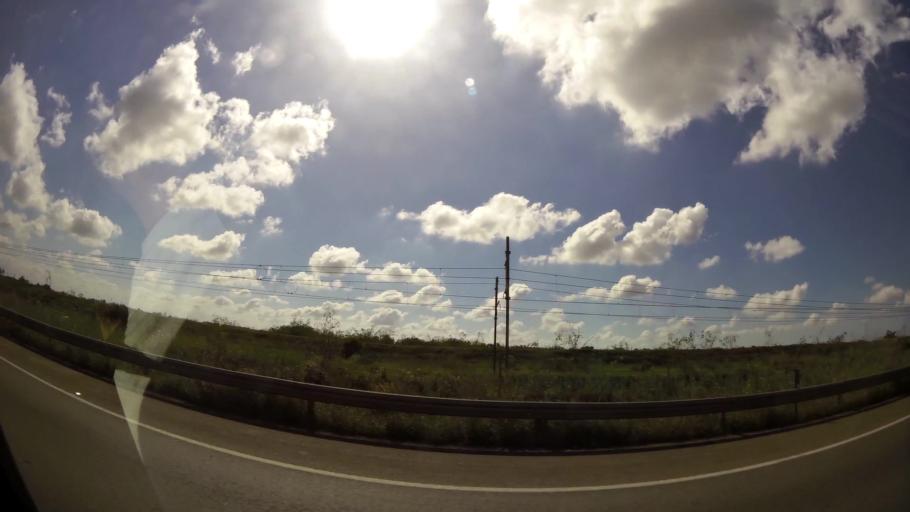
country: MA
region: Grand Casablanca
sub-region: Nouaceur
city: Bouskoura
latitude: 33.4260
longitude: -7.6275
